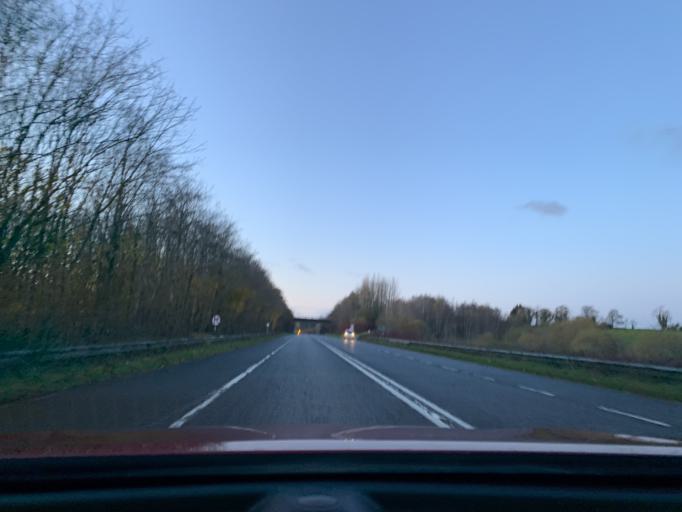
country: IE
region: Connaught
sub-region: County Leitrim
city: Carrick-on-Shannon
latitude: 53.9289
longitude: -8.0005
